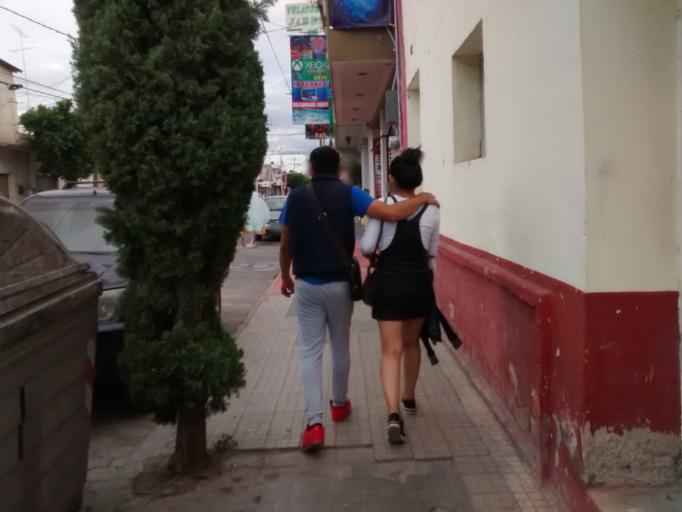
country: MX
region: Puebla
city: Tehuacan
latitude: 18.4684
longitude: -97.3915
